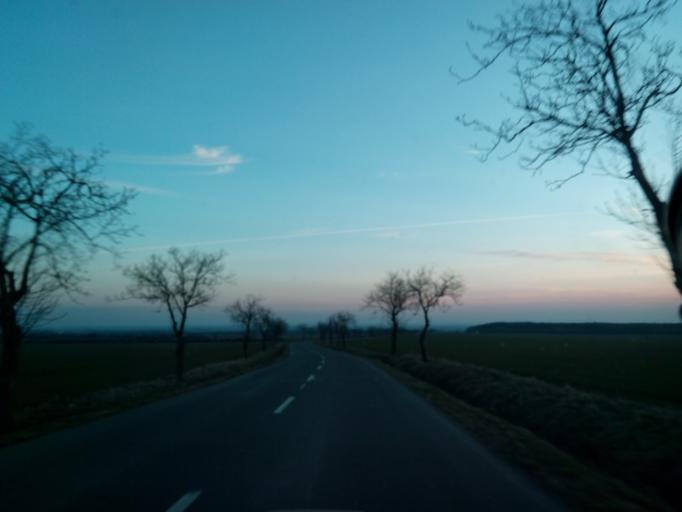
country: SK
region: Kosicky
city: Sobrance
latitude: 48.8158
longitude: 22.1668
